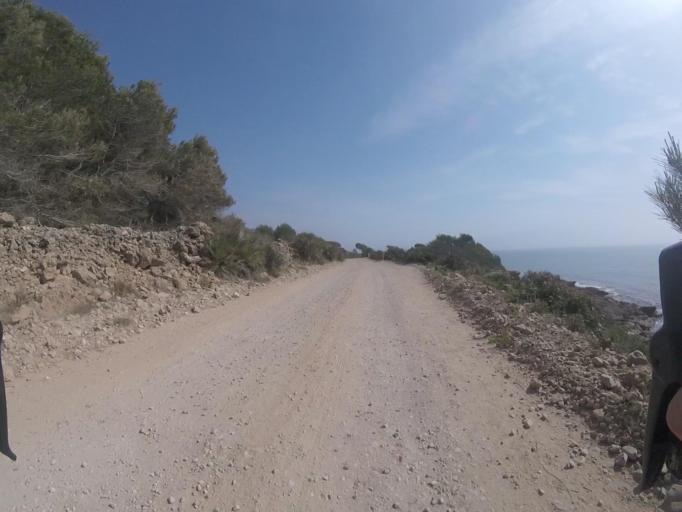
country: ES
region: Valencia
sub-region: Provincia de Castello
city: Peniscola
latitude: 40.3146
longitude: 0.3566
